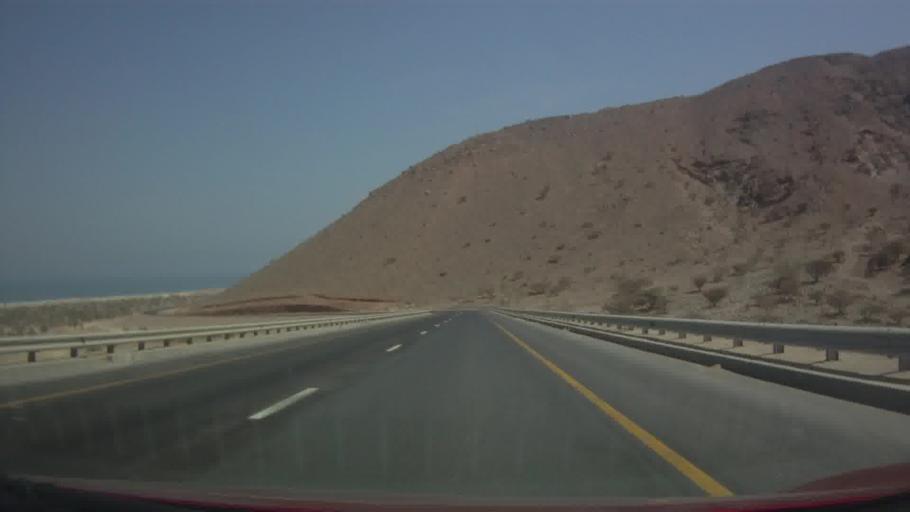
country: OM
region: Muhafazat Masqat
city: Muscat
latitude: 23.3926
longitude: 58.7921
